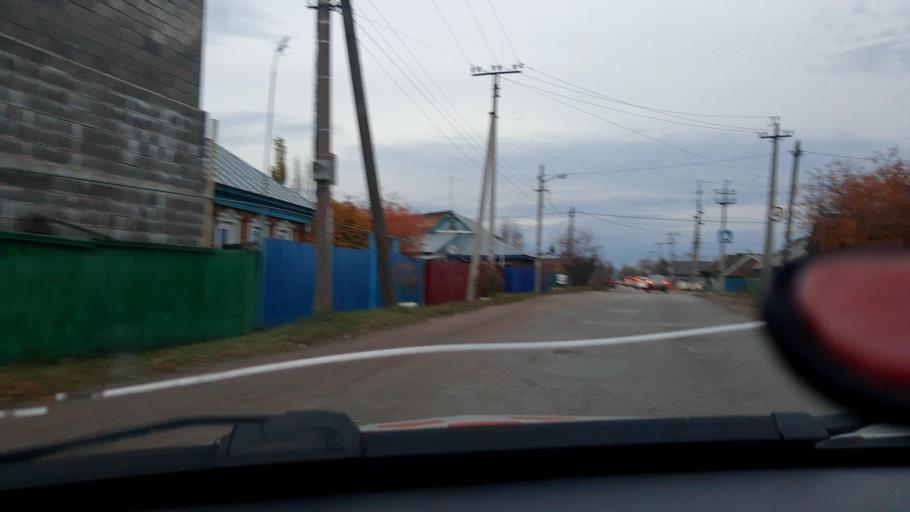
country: RU
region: Bashkortostan
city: Ufa
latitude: 54.7402
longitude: 55.9188
